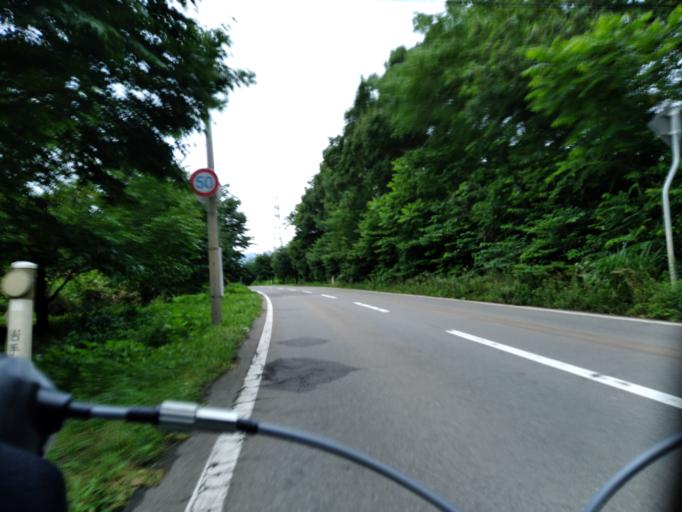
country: JP
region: Iwate
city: Morioka-shi
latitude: 39.8005
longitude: 141.1064
